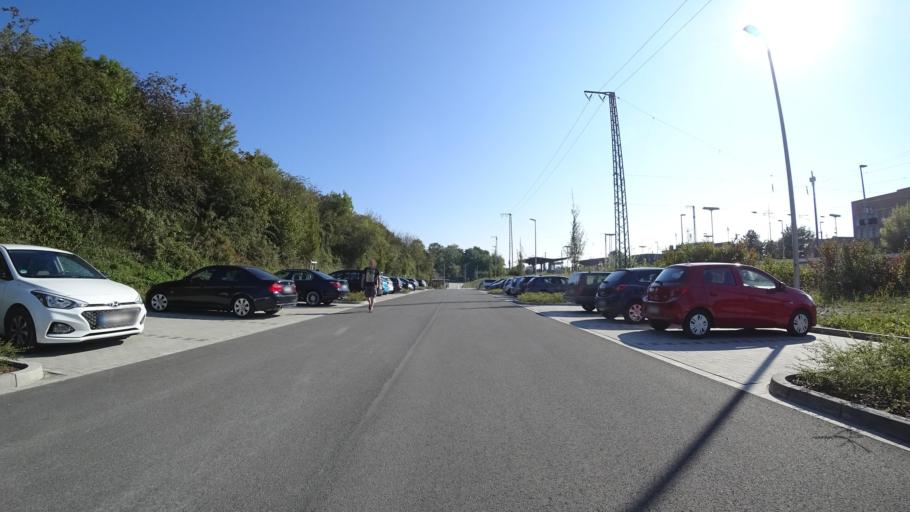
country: DE
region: North Rhine-Westphalia
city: Oelde
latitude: 51.8293
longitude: 8.1413
